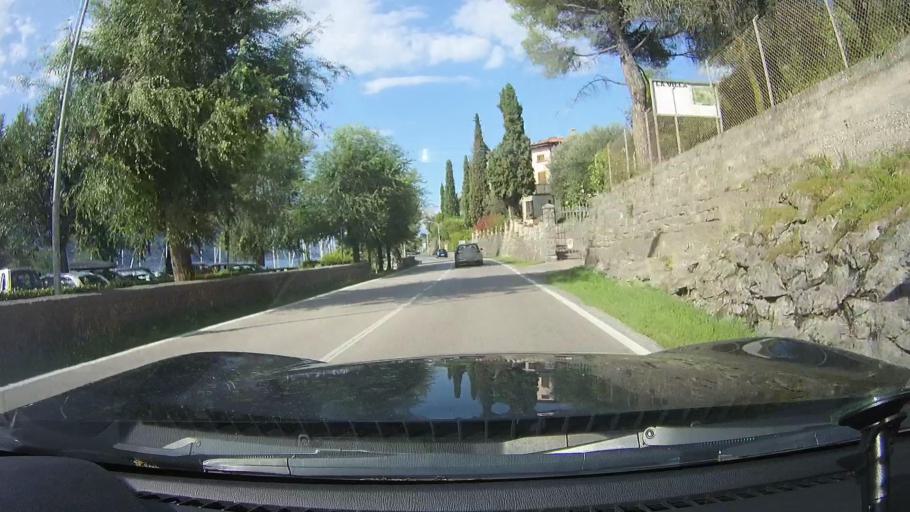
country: IT
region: Veneto
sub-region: Provincia di Verona
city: Malcesine
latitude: 45.7756
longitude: 10.8148
